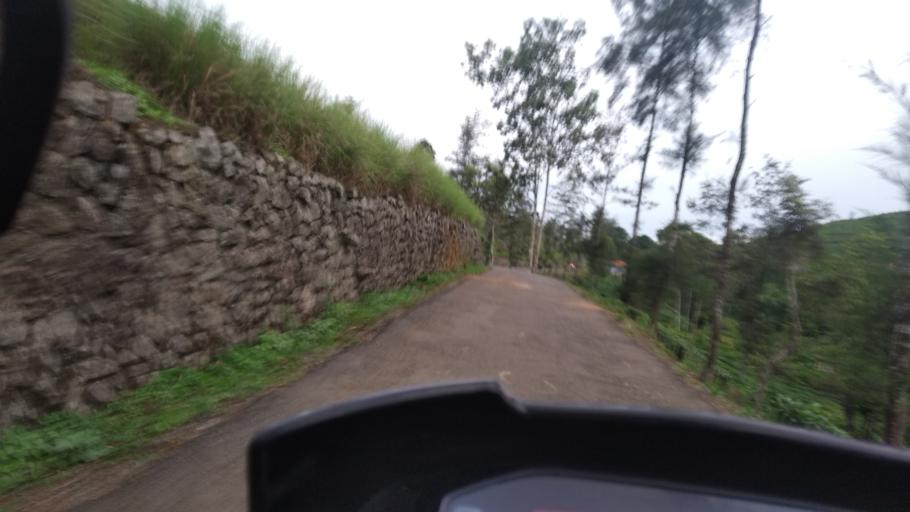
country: IN
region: Tamil Nadu
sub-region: Theni
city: Gudalur
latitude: 9.5426
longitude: 77.0467
